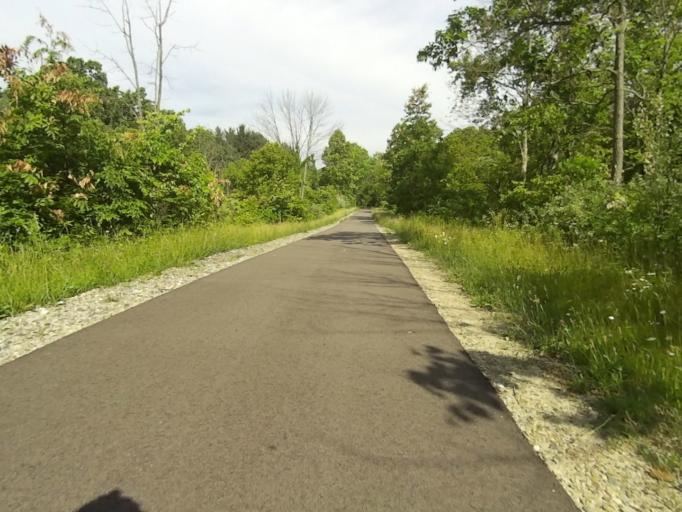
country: US
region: Ohio
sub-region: Summit County
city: Boston Heights
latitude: 41.2346
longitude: -81.4984
